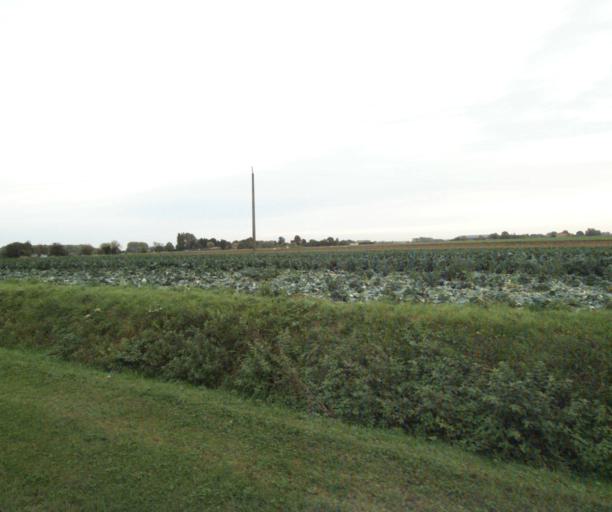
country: FR
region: Nord-Pas-de-Calais
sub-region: Departement du Nord
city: Aubers
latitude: 50.5918
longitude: 2.8251
